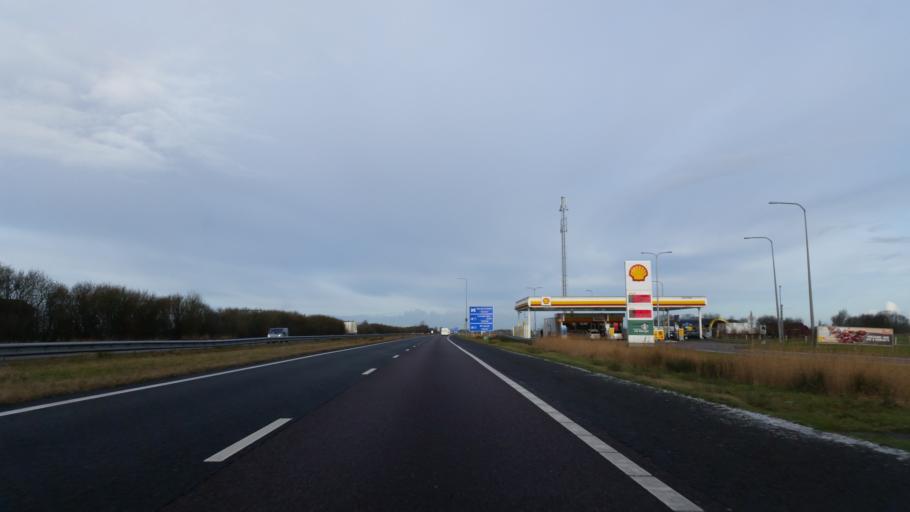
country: NL
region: Friesland
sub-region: Gemeente Boarnsterhim
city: Reduzum
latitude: 53.1273
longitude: 5.8047
